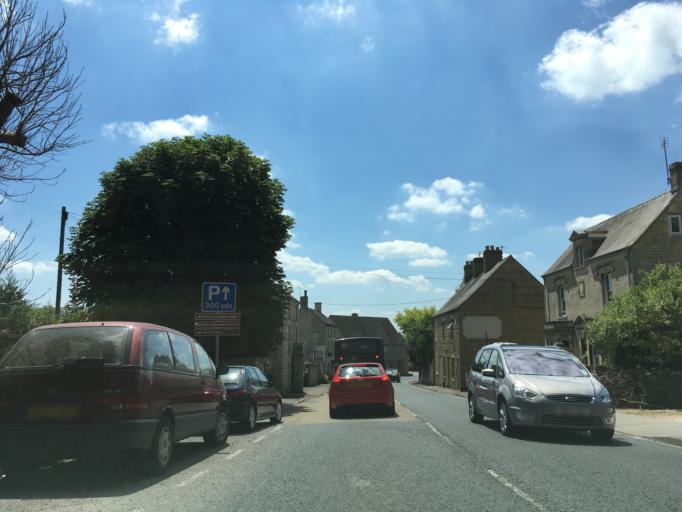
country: GB
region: England
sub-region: Gloucestershire
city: Painswick
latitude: 51.7878
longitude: -2.1927
